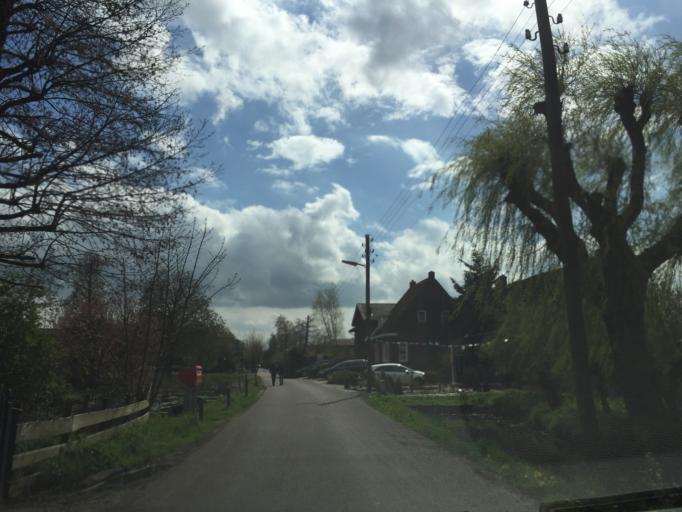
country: NL
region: South Holland
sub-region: Bodegraven-Reeuwijk
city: Reeuwijk
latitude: 52.0389
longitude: 4.7412
